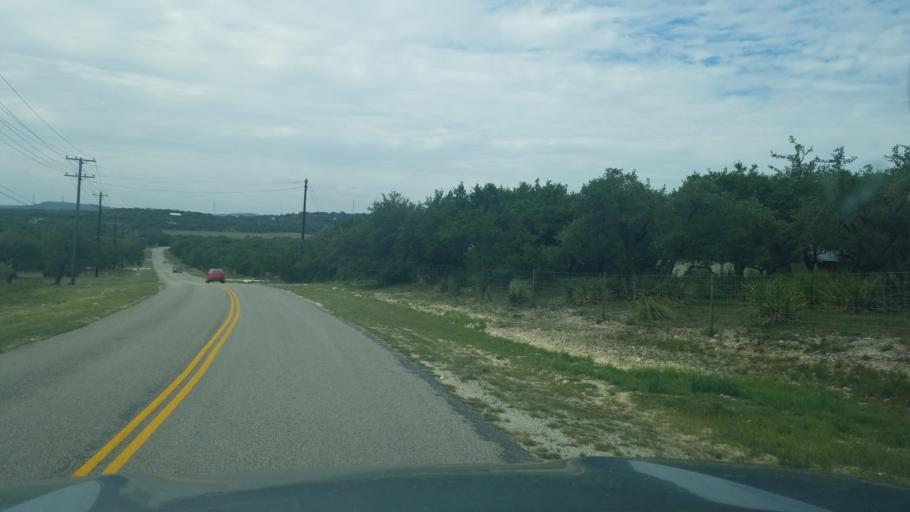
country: US
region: Texas
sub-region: Comal County
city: Bulverde
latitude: 29.7939
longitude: -98.4110
